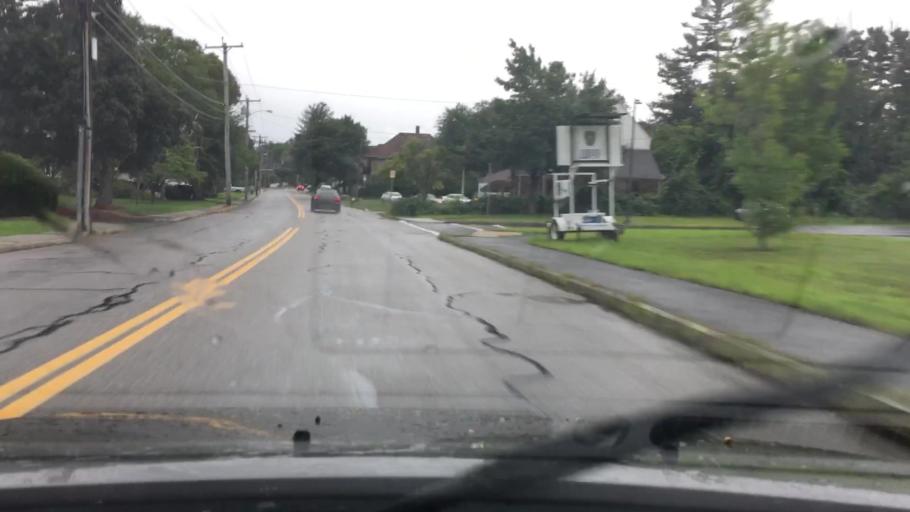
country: US
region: Massachusetts
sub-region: Worcester County
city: Milford
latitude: 42.1507
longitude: -71.5274
